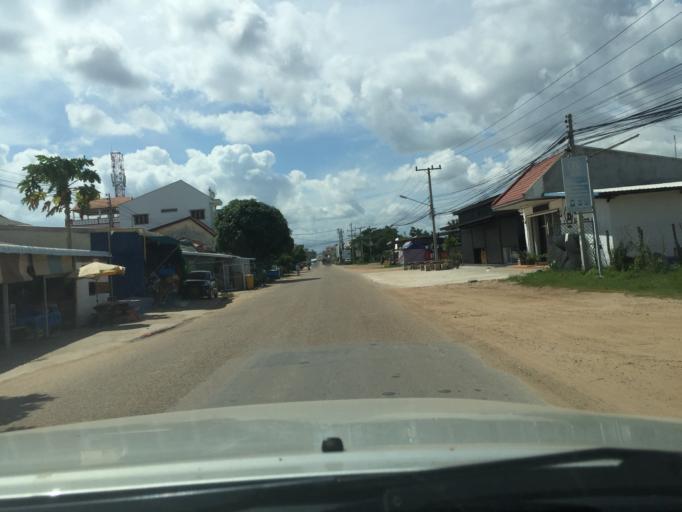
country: LA
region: Savannahkhet
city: Savannakhet
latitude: 16.5498
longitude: 104.7490
